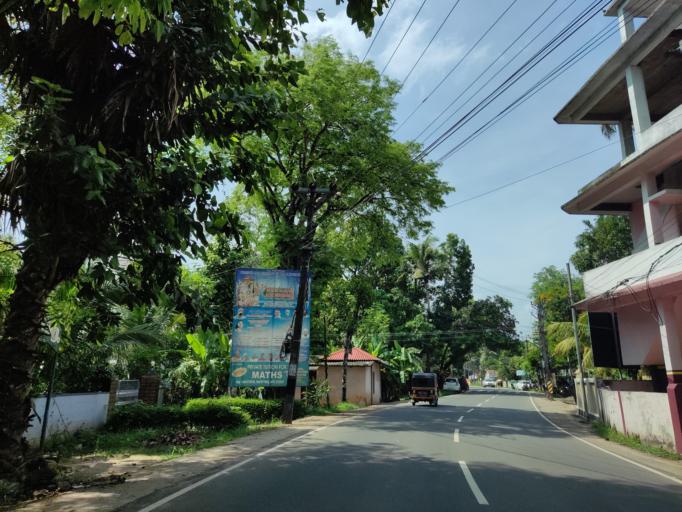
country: IN
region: Kerala
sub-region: Alappuzha
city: Mavelikara
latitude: 9.3021
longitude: 76.5336
